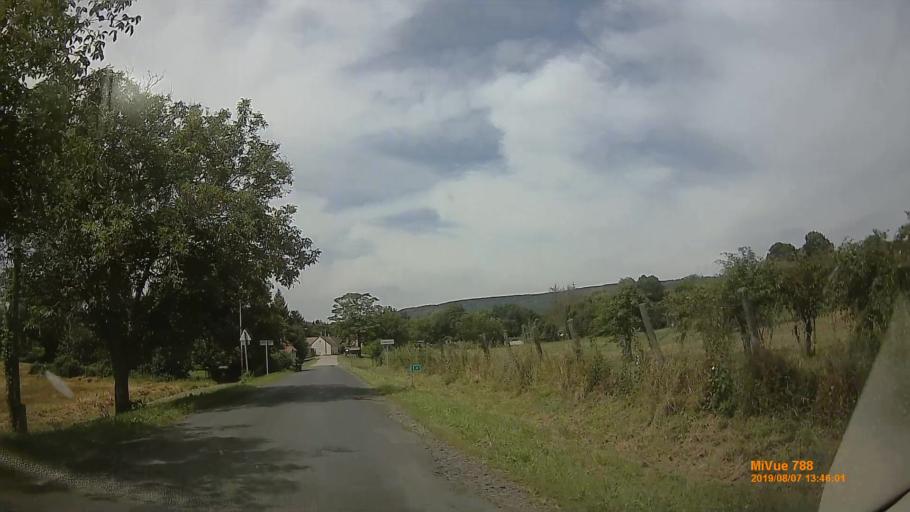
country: HU
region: Zala
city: Cserszegtomaj
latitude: 46.8840
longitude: 17.1959
